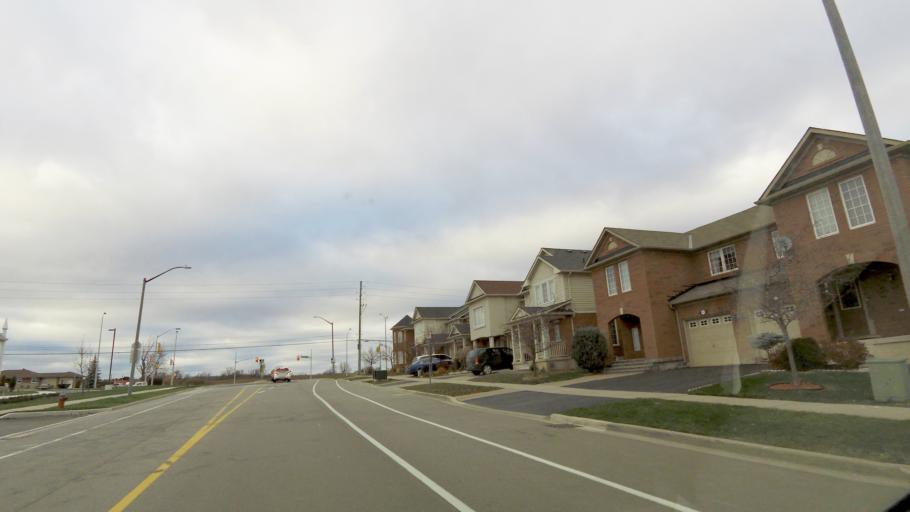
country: CA
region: Ontario
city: Burlington
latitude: 43.4324
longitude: -79.7784
